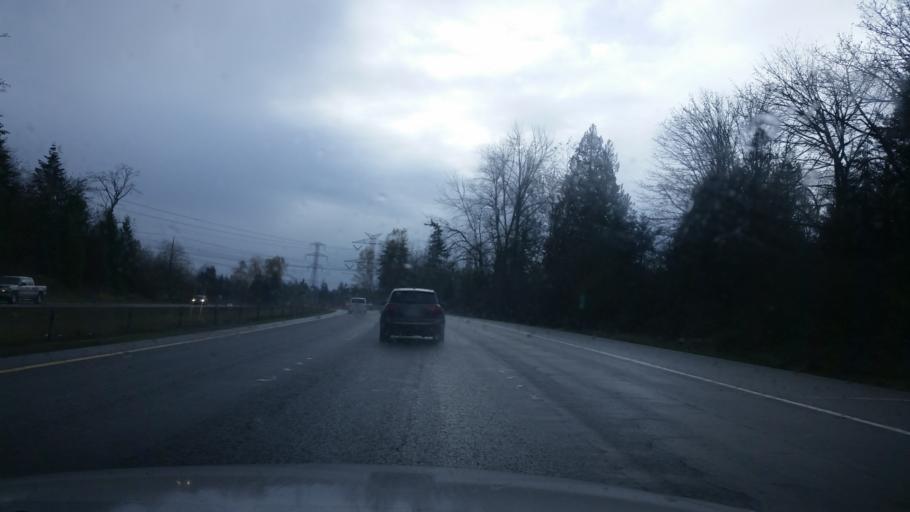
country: US
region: Washington
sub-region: King County
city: Covington
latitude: 47.3451
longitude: -122.1442
